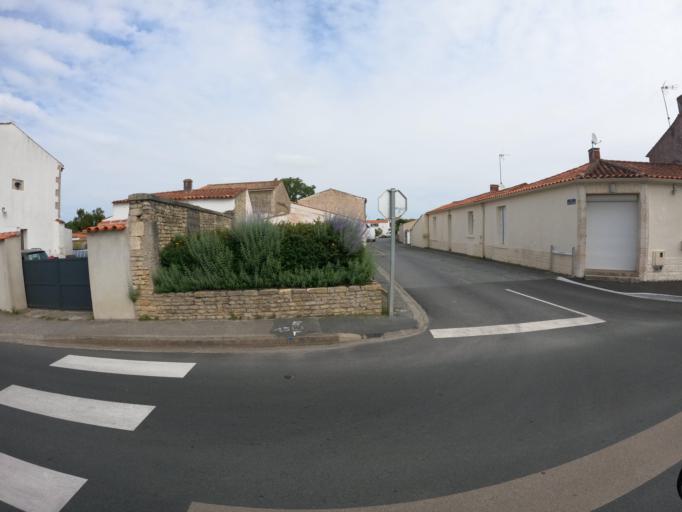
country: FR
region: Pays de la Loire
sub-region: Departement de la Vendee
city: Champagne-les-Marais
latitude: 46.3806
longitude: -1.1207
